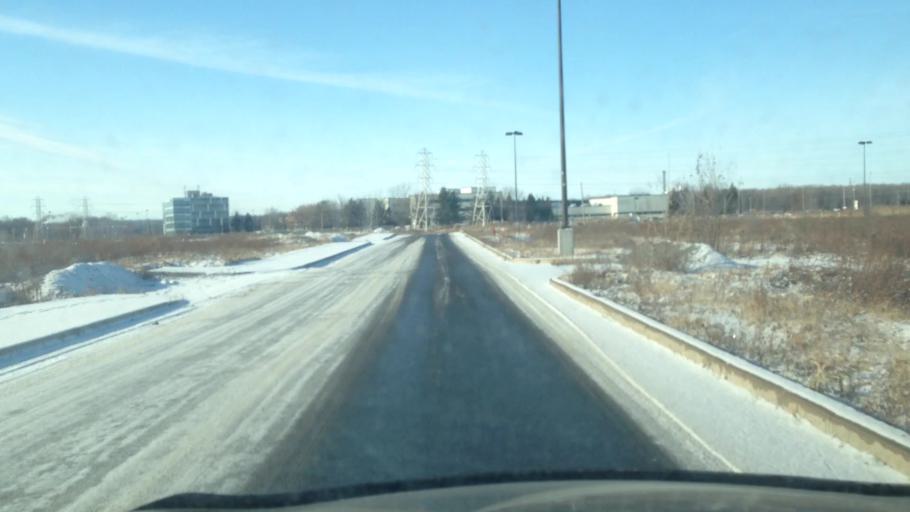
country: CA
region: Quebec
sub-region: Monteregie
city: Mercier
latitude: 45.3452
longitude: -73.7568
